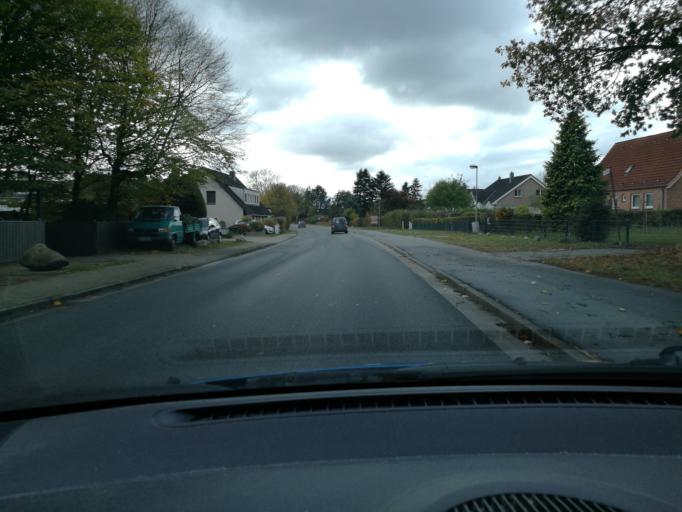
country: DE
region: Schleswig-Holstein
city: Gross Sarau
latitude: 53.7740
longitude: 10.7394
